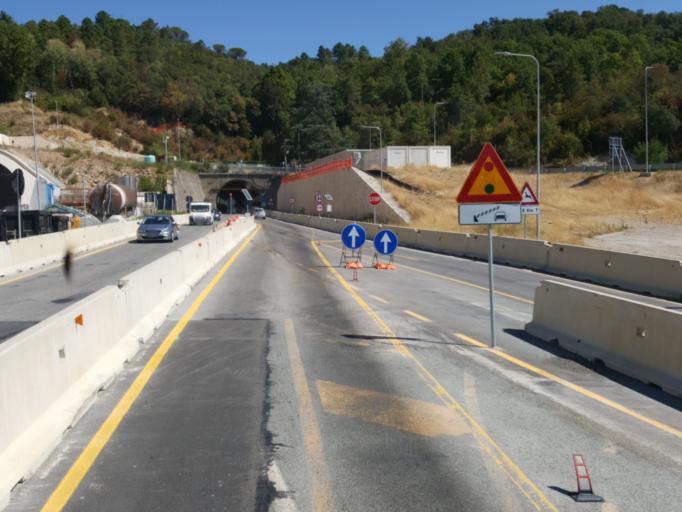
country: IT
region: Tuscany
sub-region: Provincia di Grosseto
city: Civitella Marittima
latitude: 43.0526
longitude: 11.2840
